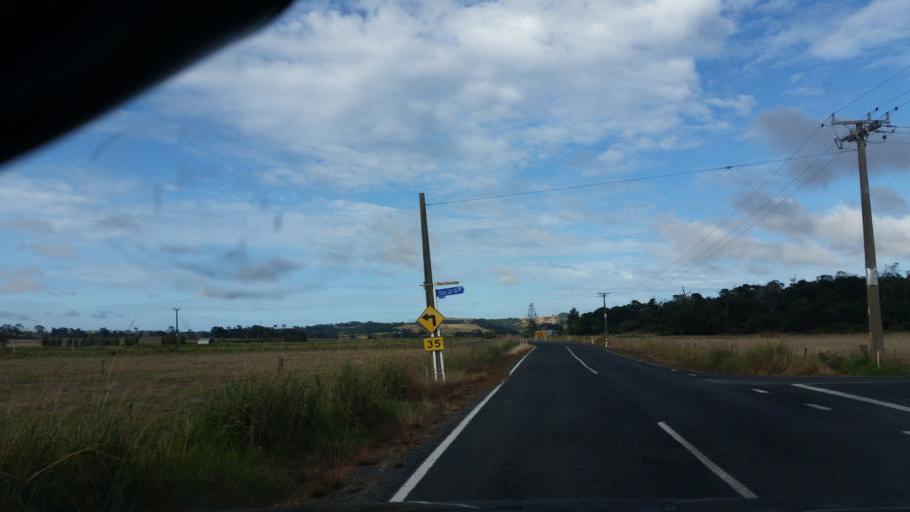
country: NZ
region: Northland
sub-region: Kaipara District
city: Dargaville
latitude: -36.0064
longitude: 173.8878
